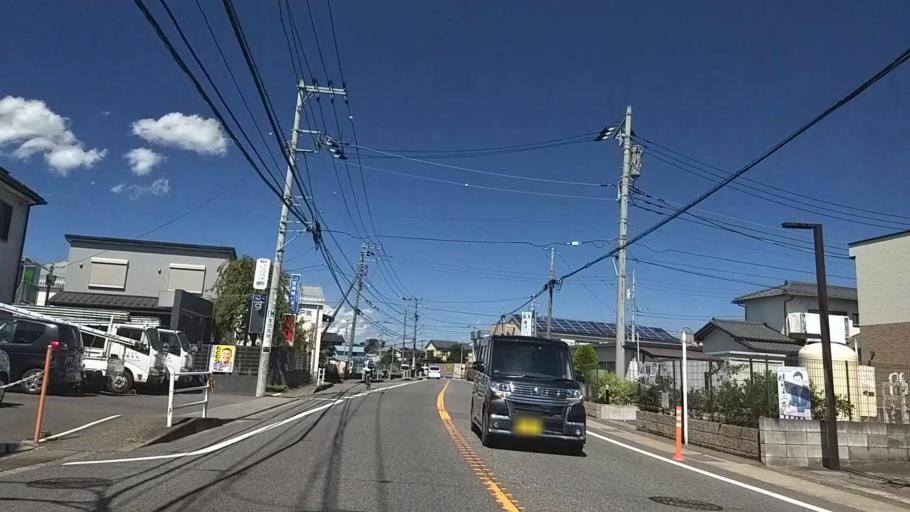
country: JP
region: Tokyo
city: Hachioji
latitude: 35.5687
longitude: 139.3217
